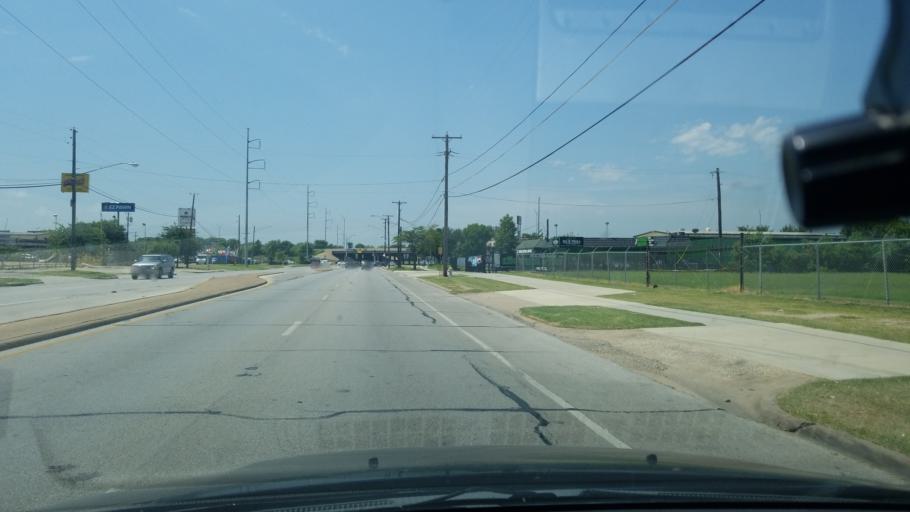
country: US
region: Texas
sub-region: Dallas County
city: Balch Springs
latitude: 32.7158
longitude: -96.6831
